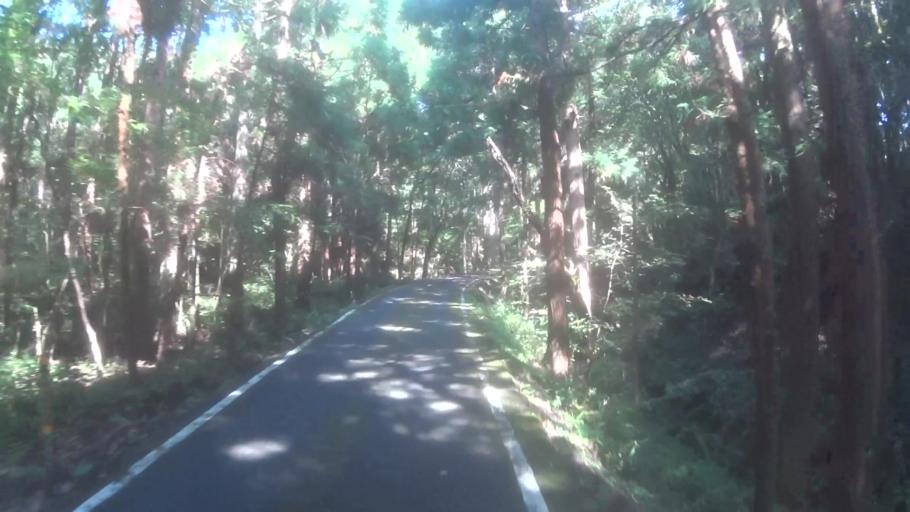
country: JP
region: Kyoto
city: Miyazu
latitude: 35.6585
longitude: 135.1225
